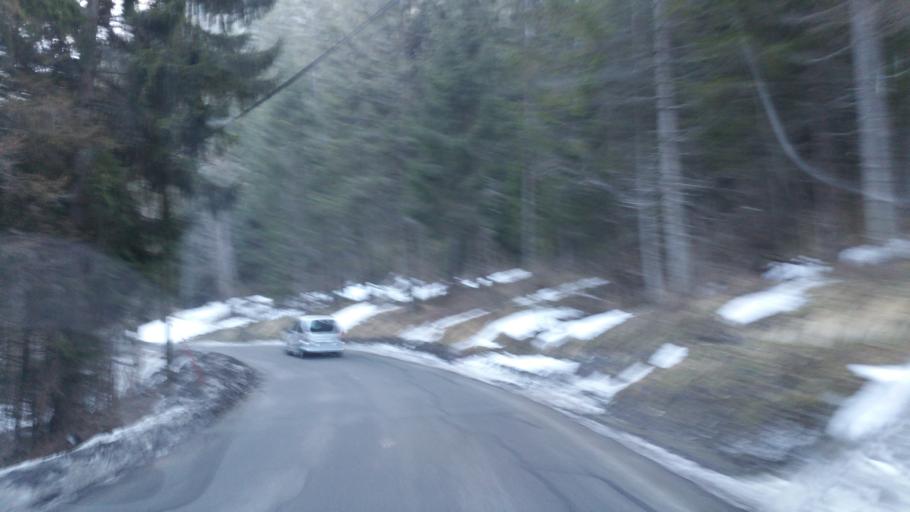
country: FR
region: Rhone-Alpes
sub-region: Departement de la Savoie
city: Saint-Jean-de-Maurienne
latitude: 45.2670
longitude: 6.3143
